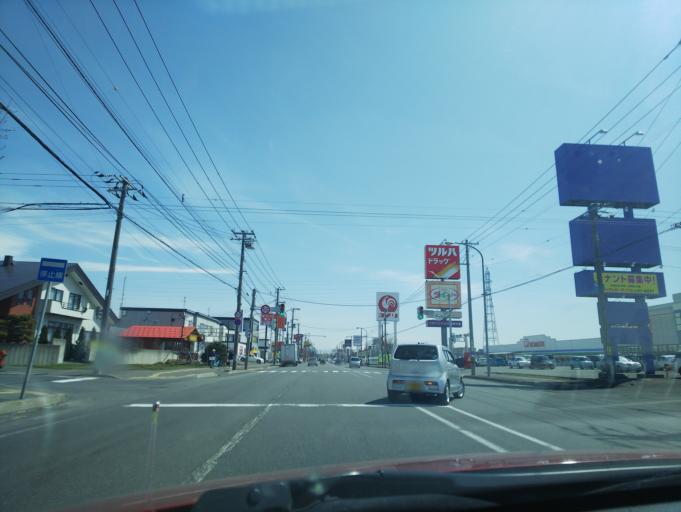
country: JP
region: Hokkaido
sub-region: Asahikawa-shi
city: Asahikawa
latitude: 43.7864
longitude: 142.4098
